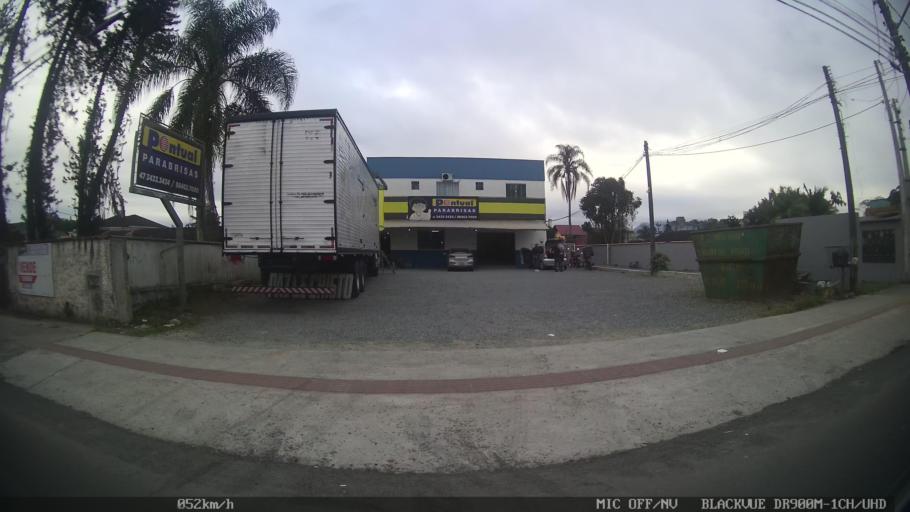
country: BR
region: Santa Catarina
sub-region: Joinville
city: Joinville
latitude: -26.2873
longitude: -48.8676
